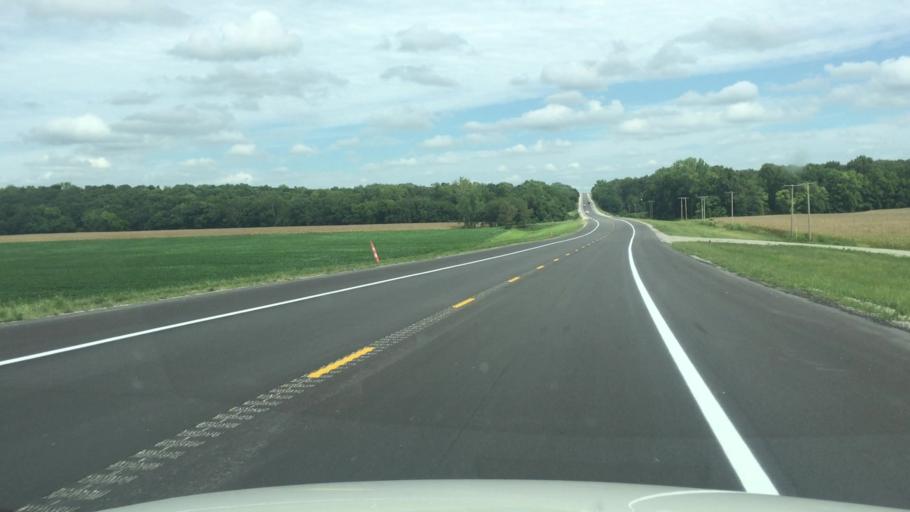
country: US
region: Kansas
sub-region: Anderson County
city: Garnett
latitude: 38.3360
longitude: -95.2489
